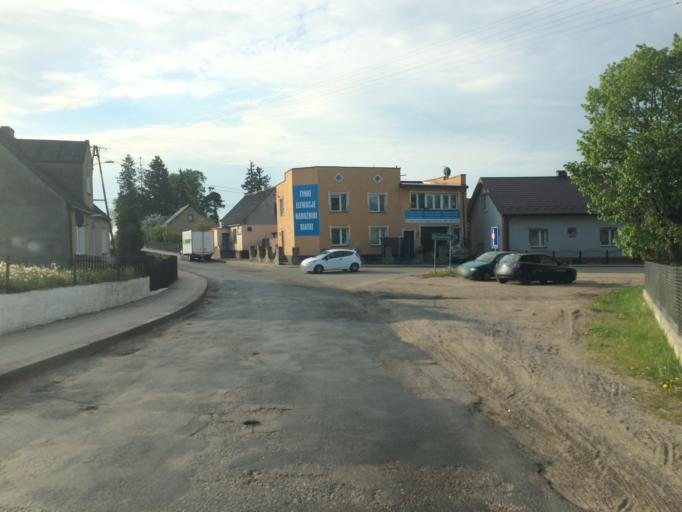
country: PL
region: Warmian-Masurian Voivodeship
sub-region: Powiat dzialdowski
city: Rybno
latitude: 53.3432
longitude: 19.9885
